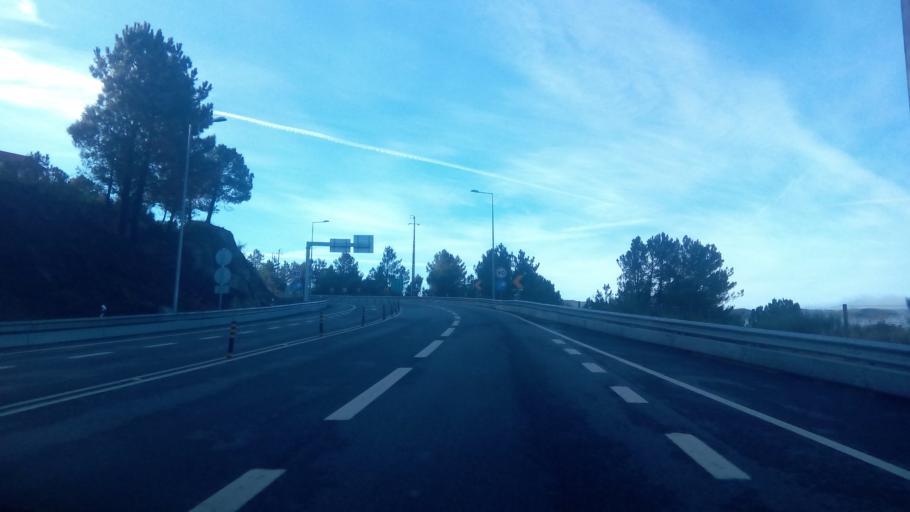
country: PT
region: Porto
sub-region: Baiao
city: Valadares
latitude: 41.2579
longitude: -7.9695
